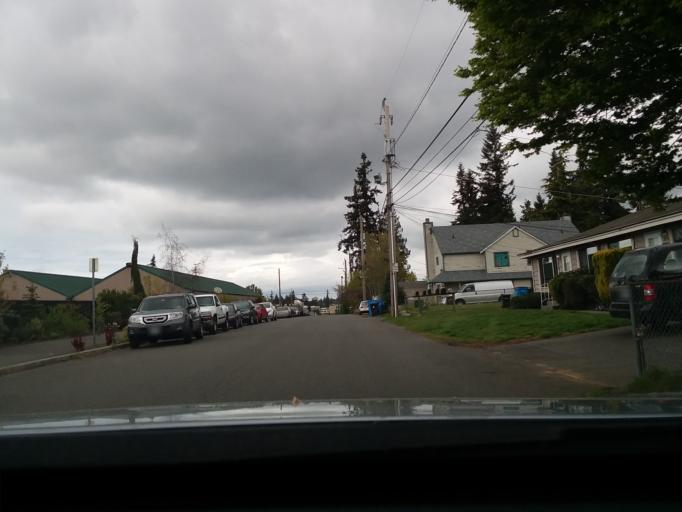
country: US
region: Washington
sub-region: King County
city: Shoreline
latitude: 47.7643
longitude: -122.3440
